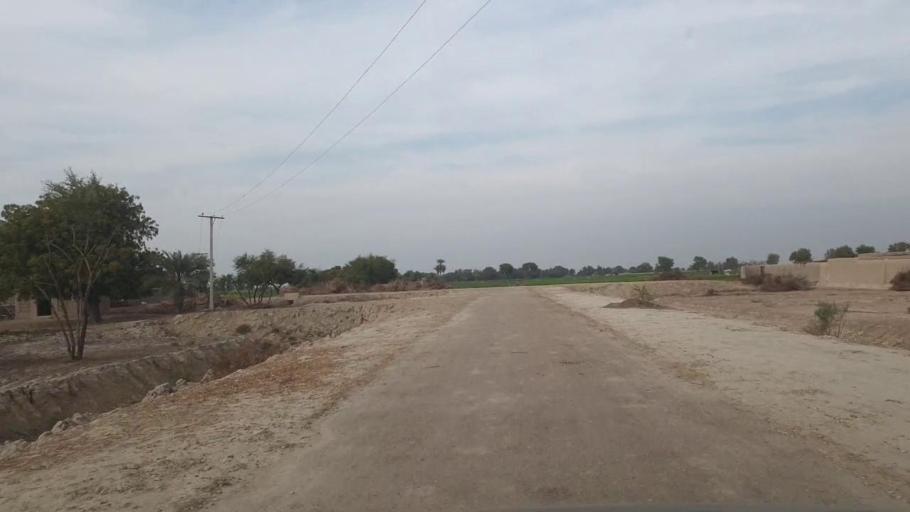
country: PK
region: Sindh
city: Shahpur Chakar
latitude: 26.1111
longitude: 68.5262
